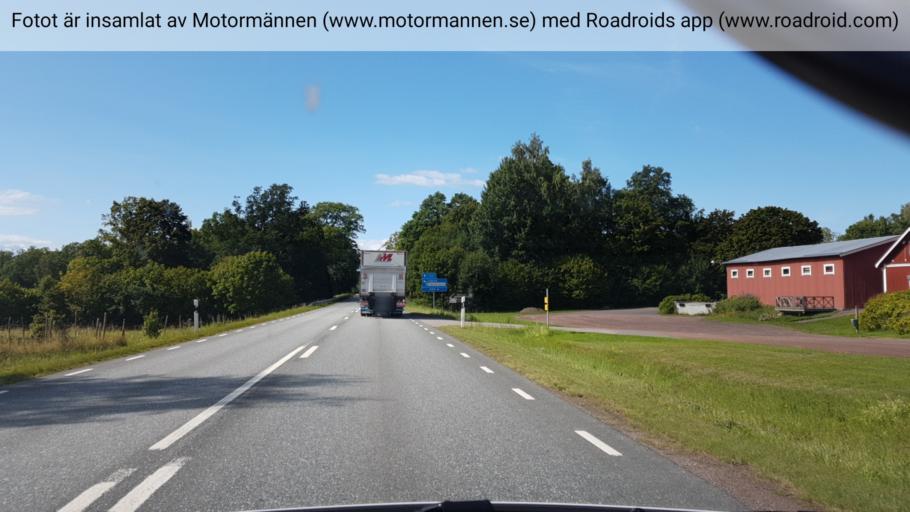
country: SE
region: Joenkoeping
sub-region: Jonkopings Kommun
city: Asa
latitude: 58.0046
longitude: 14.6007
